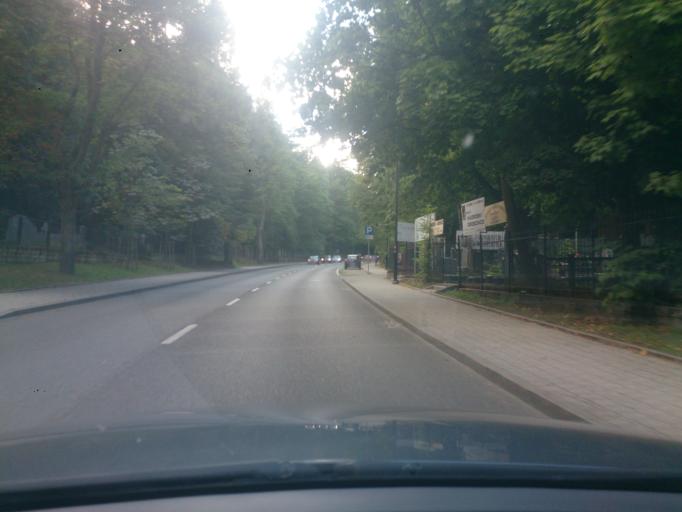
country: PL
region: Pomeranian Voivodeship
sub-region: Sopot
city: Sopot
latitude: 54.4509
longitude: 18.5478
